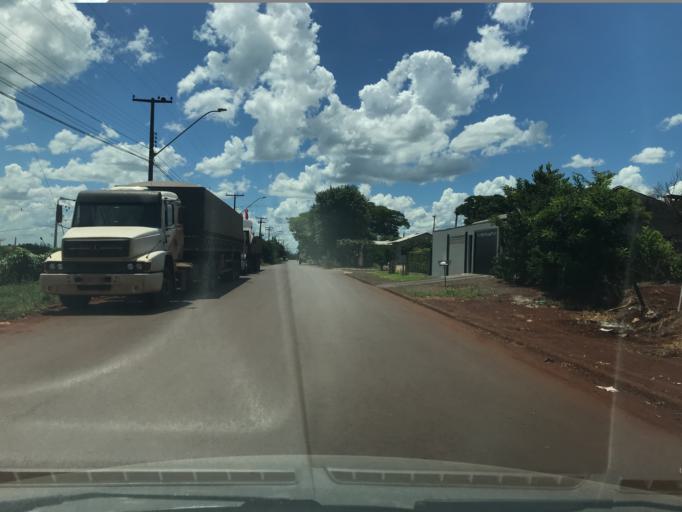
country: BR
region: Parana
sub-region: Palotina
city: Palotina
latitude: -24.2732
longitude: -53.8485
